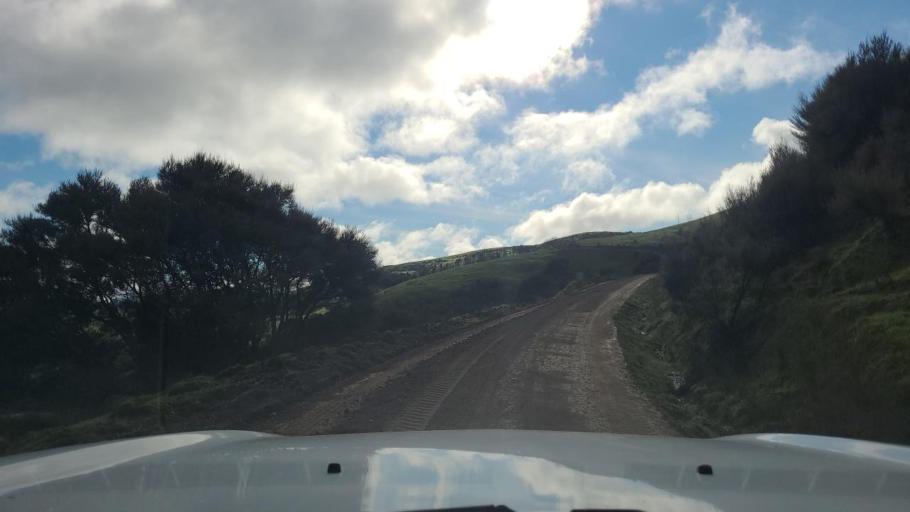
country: NZ
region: Wellington
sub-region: South Wairarapa District
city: Waipawa
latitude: -41.2446
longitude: 175.6894
